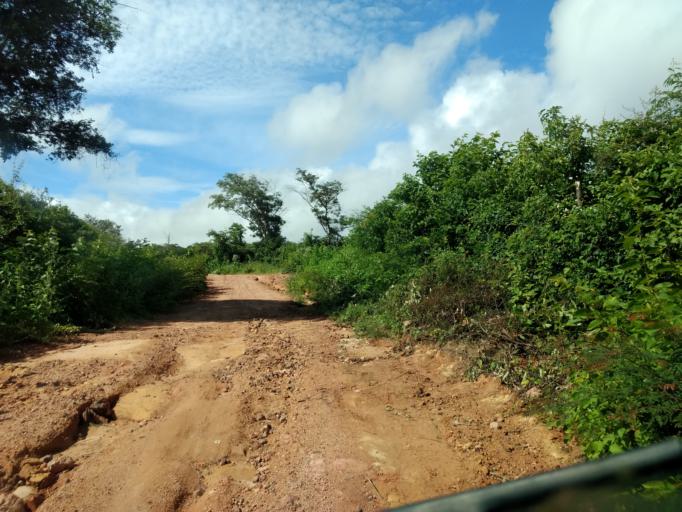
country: BR
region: Ceara
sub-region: Crateus
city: Crateus
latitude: -5.2189
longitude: -40.9473
